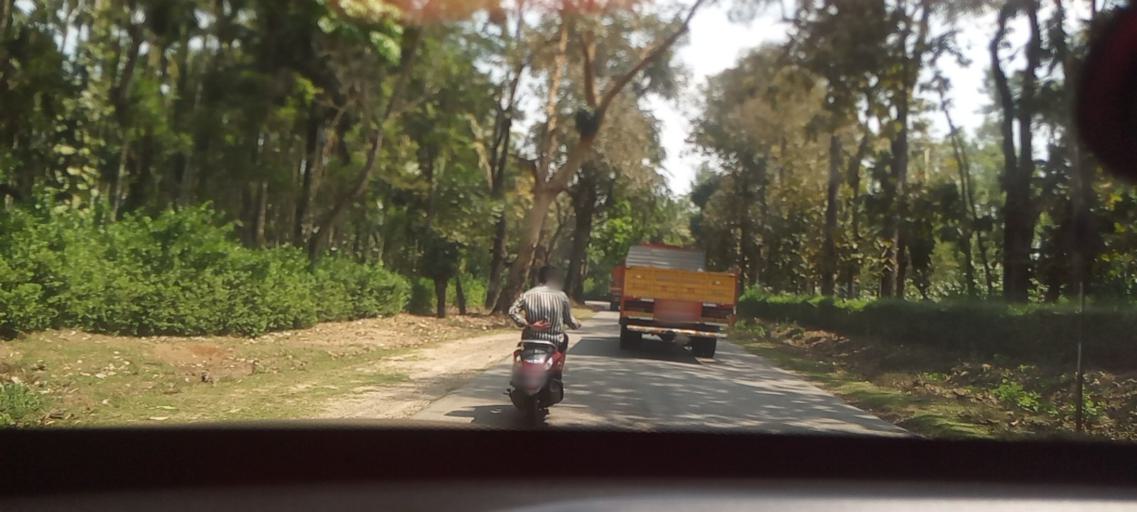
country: IN
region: Karnataka
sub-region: Chikmagalur
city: Chikmagalur
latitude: 13.3330
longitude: 75.5552
